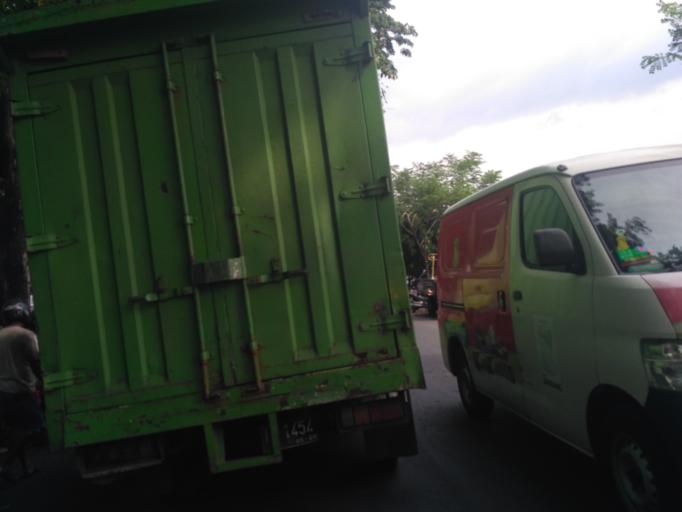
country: ID
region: Central Java
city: Semarang
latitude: -6.9761
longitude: 110.4019
